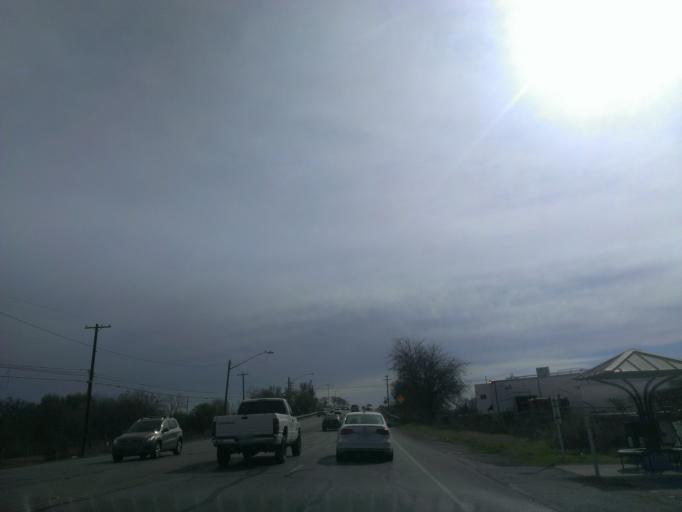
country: US
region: Texas
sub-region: Travis County
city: Austin
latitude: 30.2652
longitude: -97.6955
